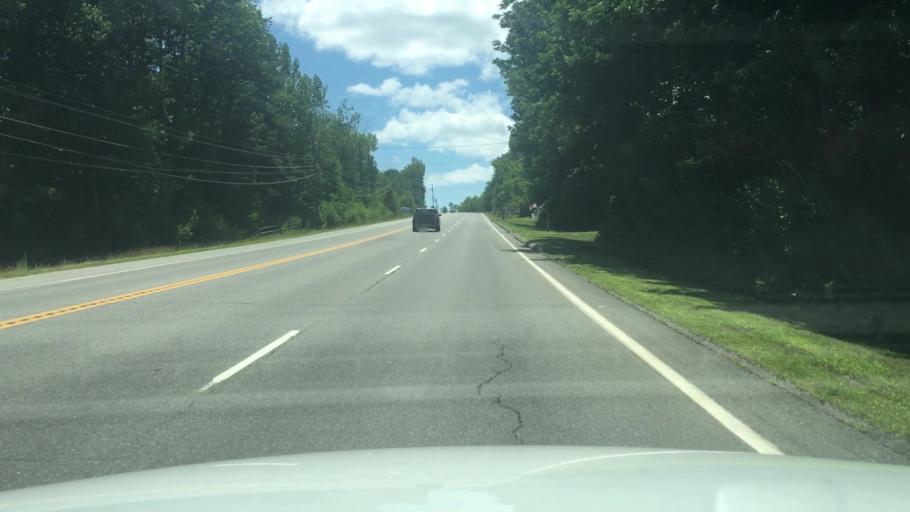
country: US
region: Maine
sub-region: Waldo County
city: Northport
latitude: 44.3645
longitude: -68.9781
